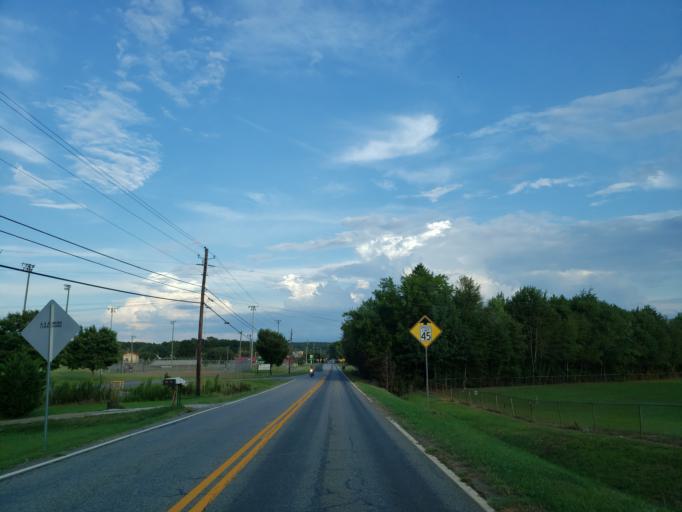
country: US
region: Georgia
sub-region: Bartow County
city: Cartersville
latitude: 34.2349
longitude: -84.8686
